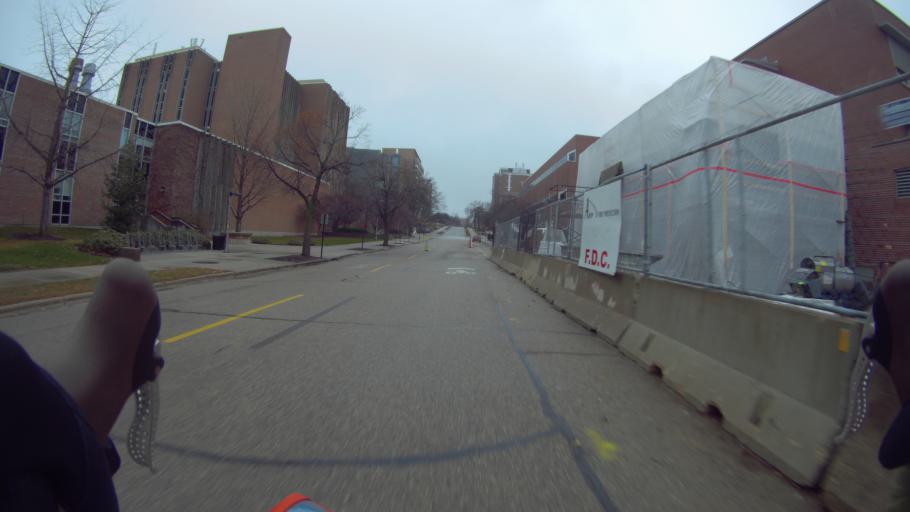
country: US
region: Wisconsin
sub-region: Dane County
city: Madison
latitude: 43.0752
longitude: -89.4144
